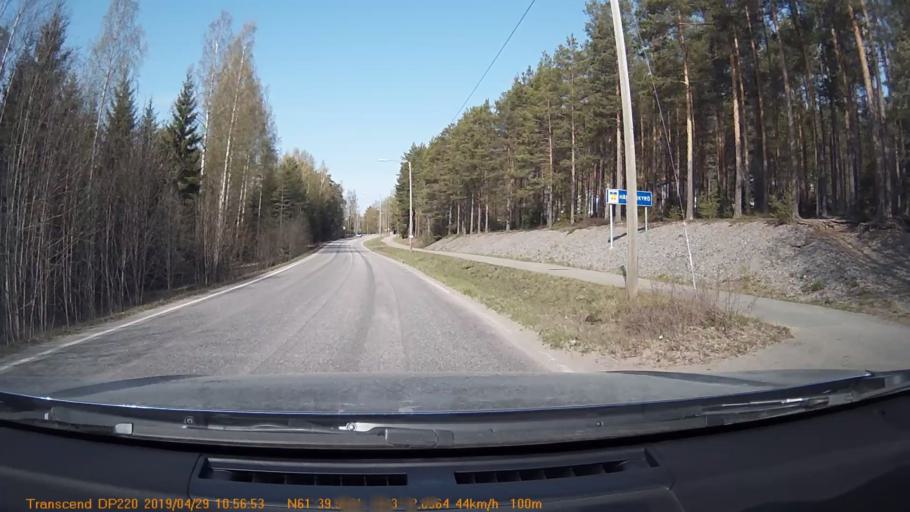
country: FI
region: Pirkanmaa
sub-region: Tampere
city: Haemeenkyroe
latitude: 61.6655
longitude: 23.2142
